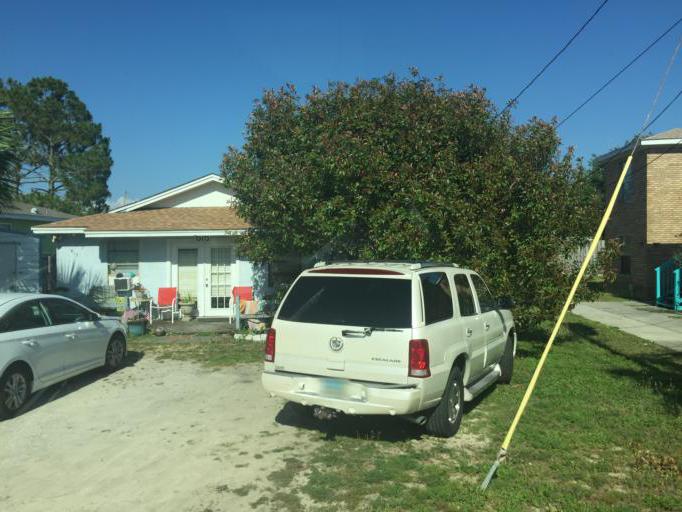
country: US
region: Florida
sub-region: Bay County
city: Panama City Beach
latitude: 30.1970
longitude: -85.8390
